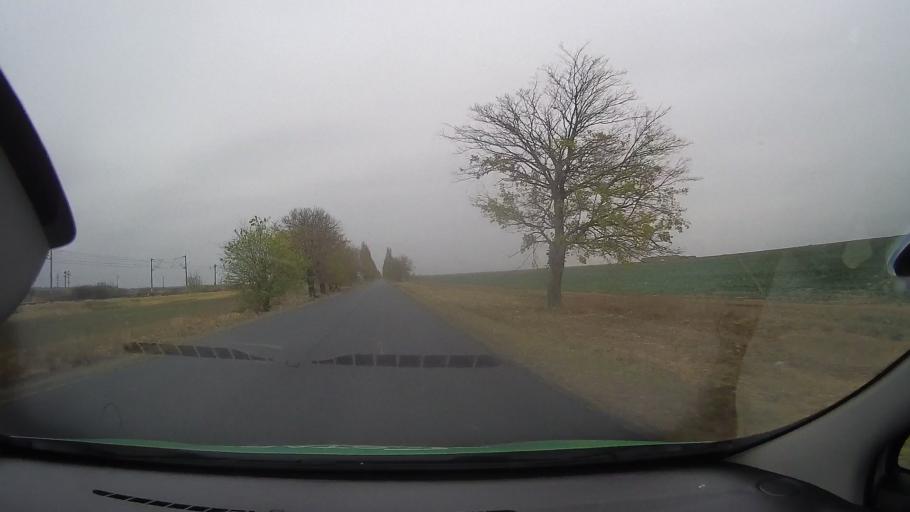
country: RO
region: Ialomita
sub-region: Comuna Valea Ciorii
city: Valea Ciorii
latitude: 44.7069
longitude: 27.5942
